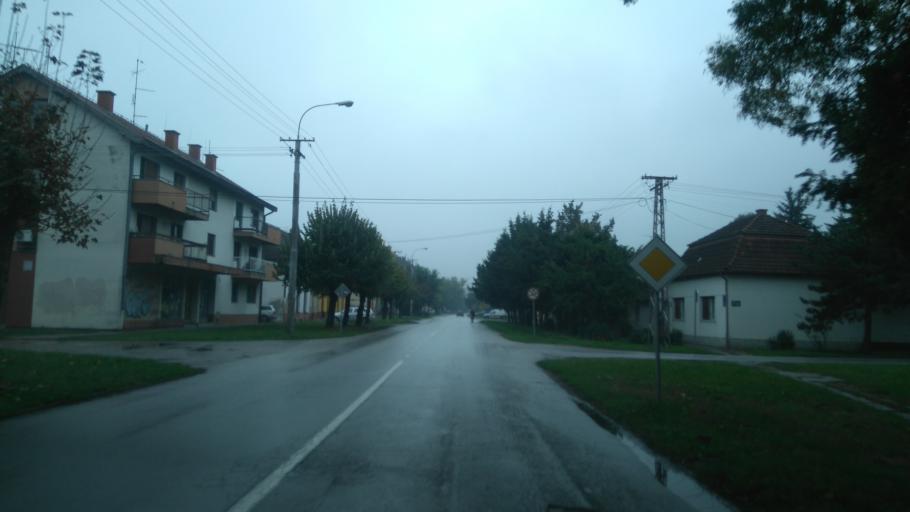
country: RS
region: Autonomna Pokrajina Vojvodina
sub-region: Juznobacki Okrug
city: Becej
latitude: 45.6209
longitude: 20.0392
